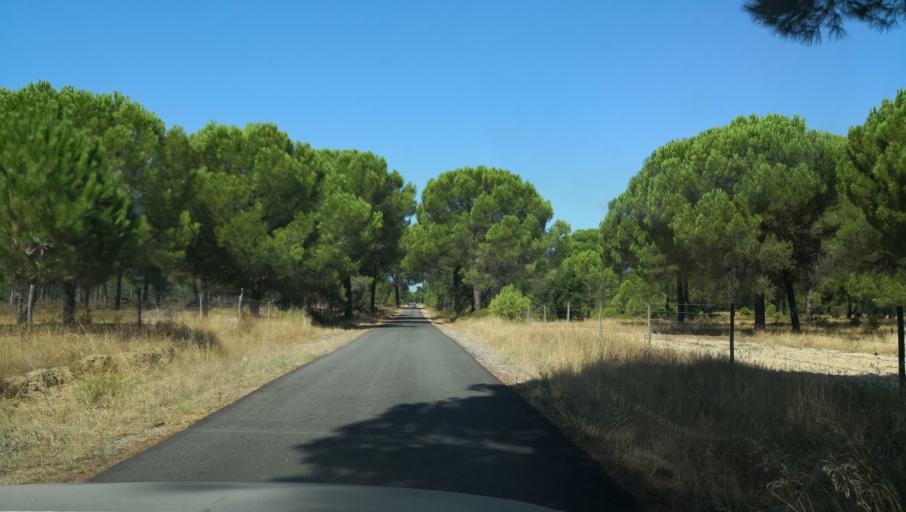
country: PT
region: Setubal
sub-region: Alcacer do Sal
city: Alcacer do Sal
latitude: 38.2599
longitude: -8.3076
